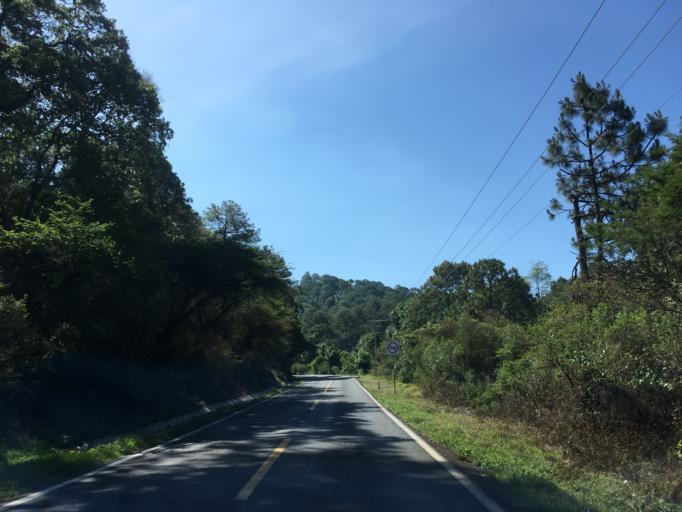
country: MX
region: Michoacan
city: Tzitzio
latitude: 19.6534
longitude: -100.9922
